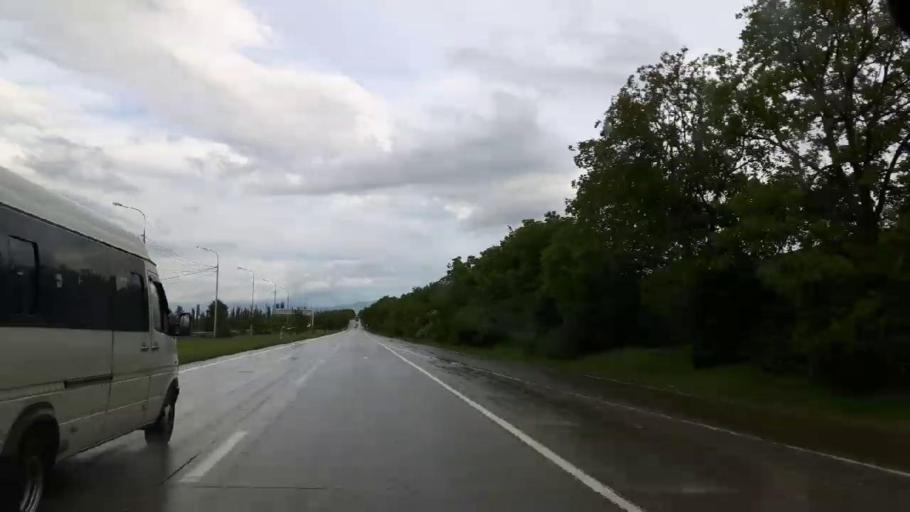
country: GE
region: Shida Kartli
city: Kaspi
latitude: 41.9619
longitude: 44.4754
